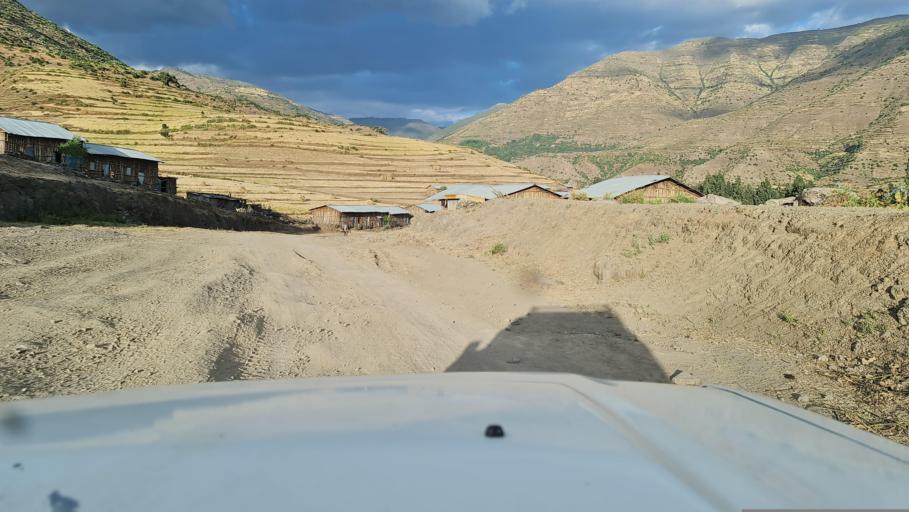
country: ET
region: Amhara
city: Debark'
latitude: 13.0362
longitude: 38.0437
